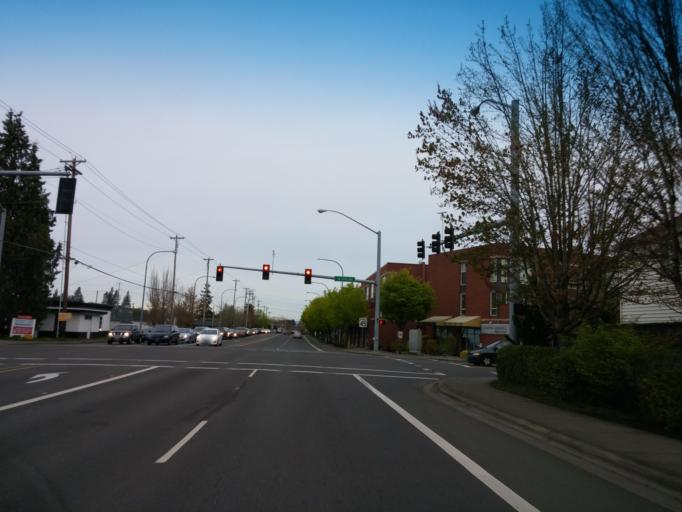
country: US
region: Oregon
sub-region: Washington County
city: Aloha
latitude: 45.5126
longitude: -122.8516
